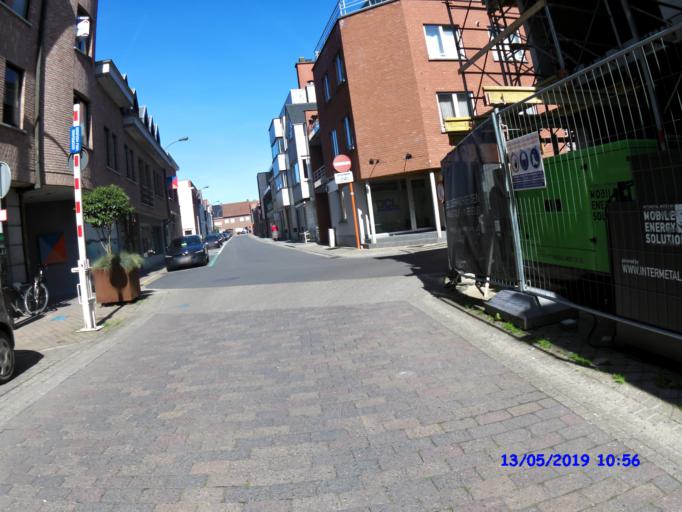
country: BE
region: Flanders
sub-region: Provincie West-Vlaanderen
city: Waregem
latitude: 50.8853
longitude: 3.4287
